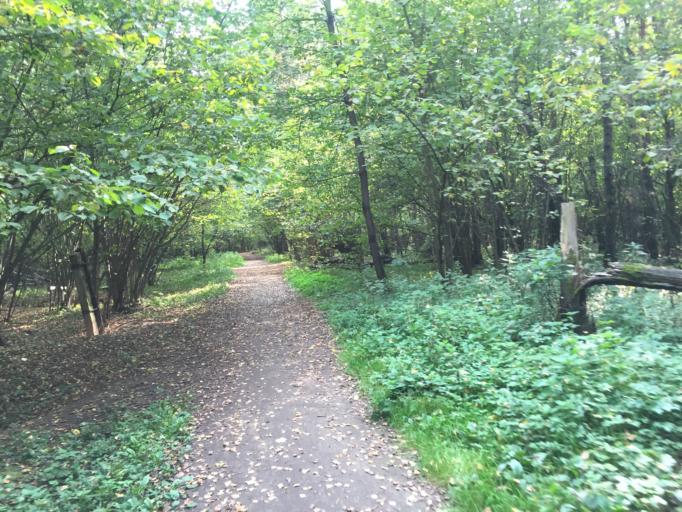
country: RU
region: Moscow
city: Babushkin
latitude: 55.8689
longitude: 37.7299
